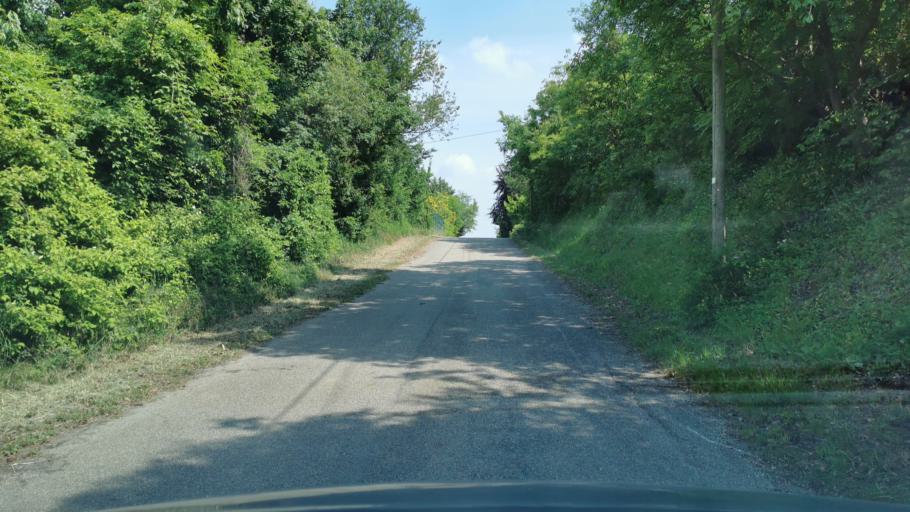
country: IT
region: Piedmont
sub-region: Provincia di Asti
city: Grazzano Badoglio
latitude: 45.0553
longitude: 8.3135
